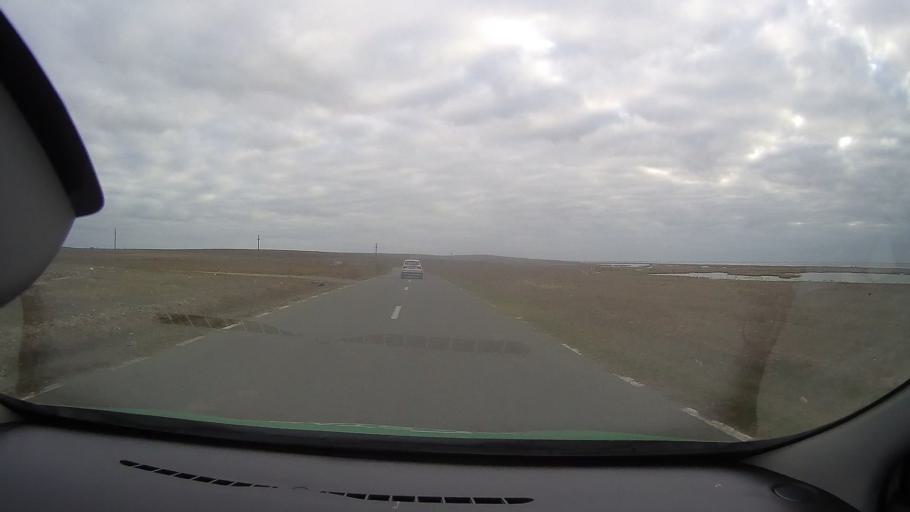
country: RO
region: Tulcea
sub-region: Comuna Jurilovca
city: Jurilovca
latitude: 44.7607
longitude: 28.8878
